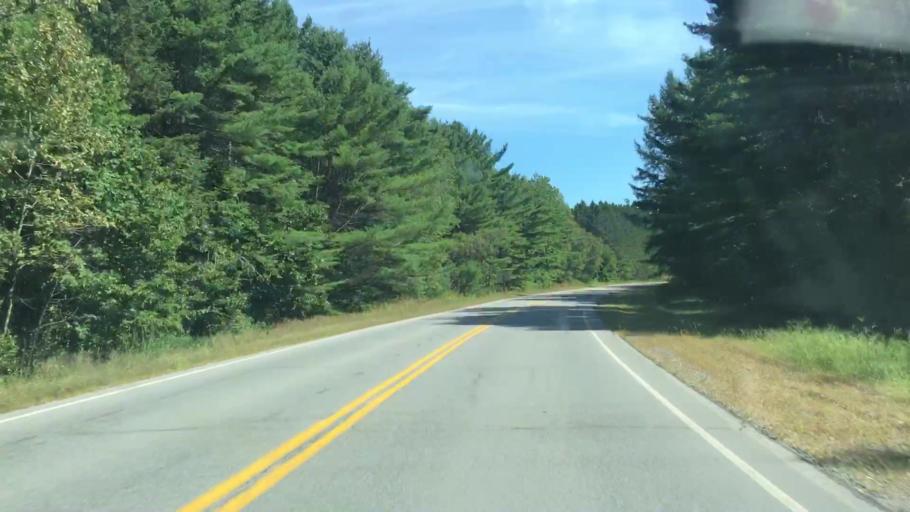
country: US
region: Maine
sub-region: Piscataquis County
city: Milo
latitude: 45.2298
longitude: -68.9362
